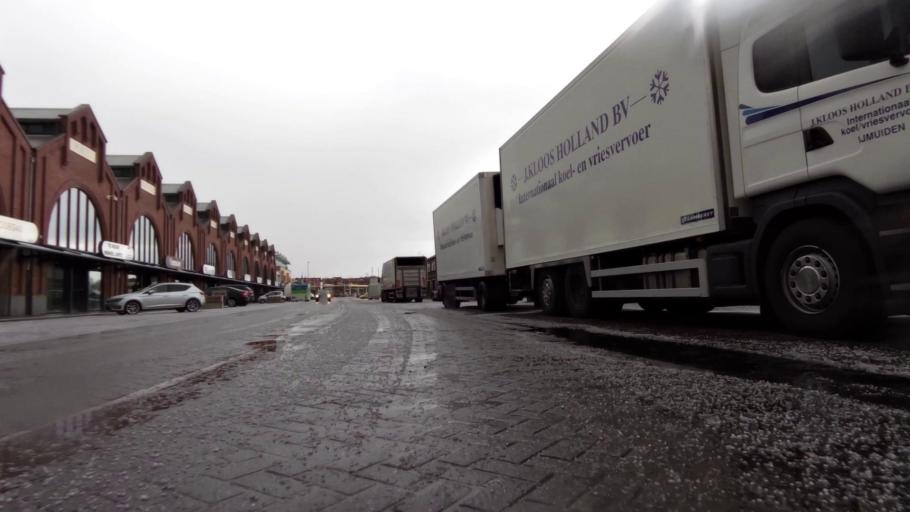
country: NL
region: North Holland
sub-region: Gemeente Velsen
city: Velsen-Zuid
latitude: 52.4594
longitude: 4.5944
